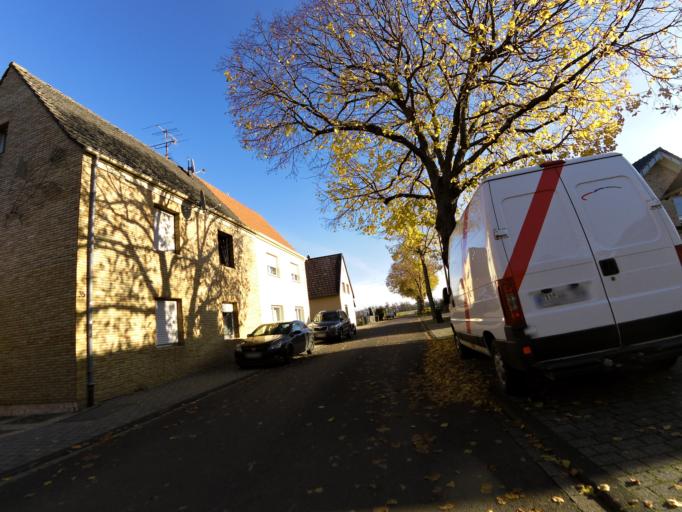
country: DE
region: North Rhine-Westphalia
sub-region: Regierungsbezirk Koln
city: Euskirchen
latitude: 50.6372
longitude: 6.8629
